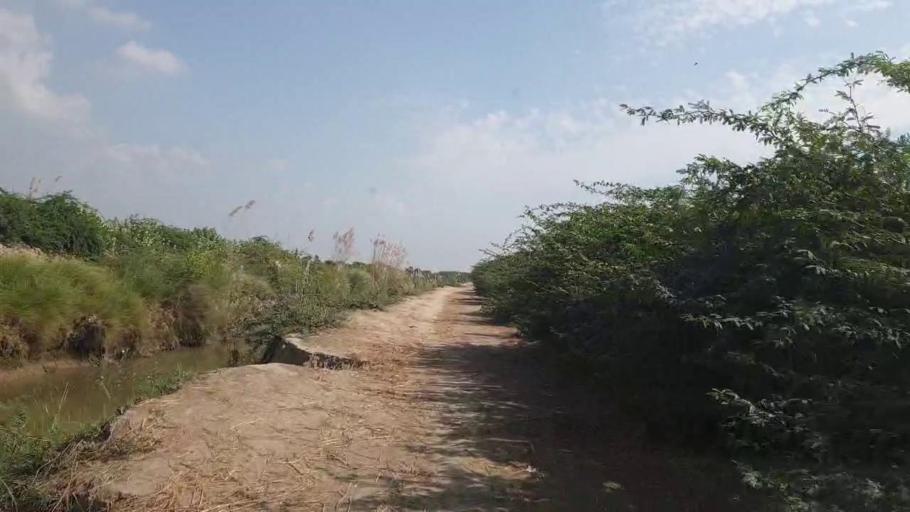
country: PK
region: Sindh
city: Badin
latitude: 24.4774
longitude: 68.5991
